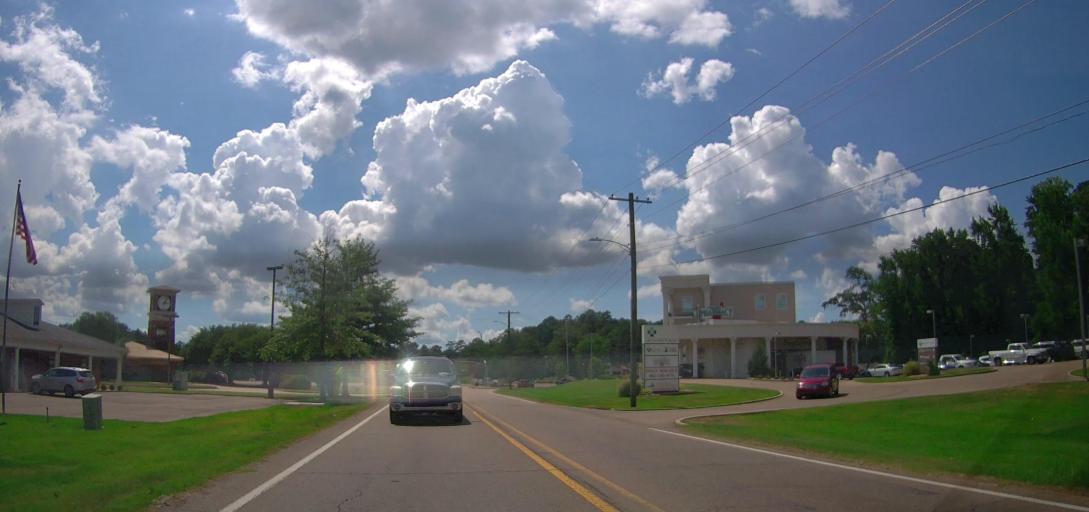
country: US
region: Mississippi
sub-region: Lowndes County
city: Columbus
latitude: 33.5385
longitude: -88.4369
